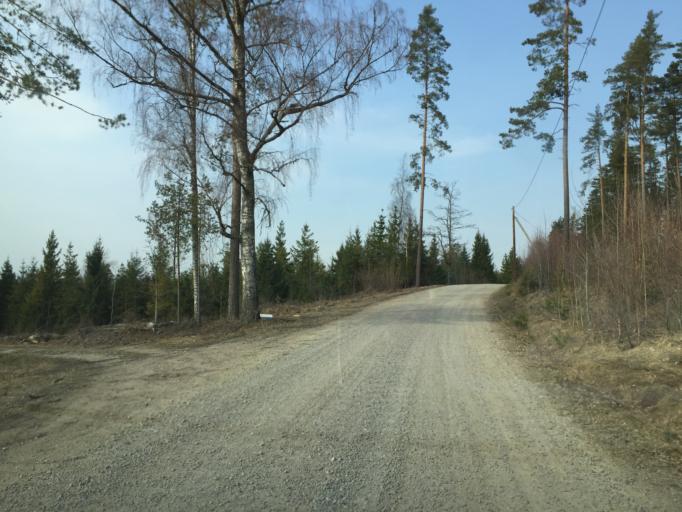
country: SE
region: Soedermanland
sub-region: Vingakers Kommun
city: Vingaker
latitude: 59.0105
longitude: 15.7818
